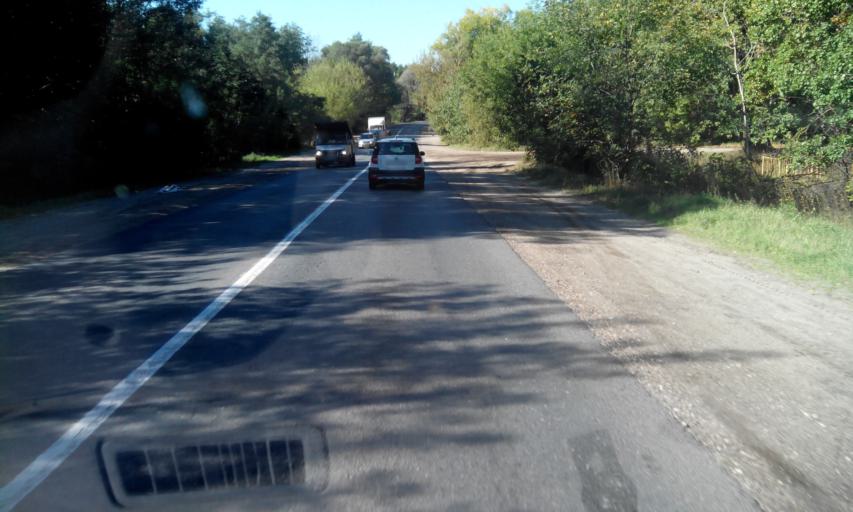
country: RU
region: Penza
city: Zarechnyy
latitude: 53.2104
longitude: 45.1243
